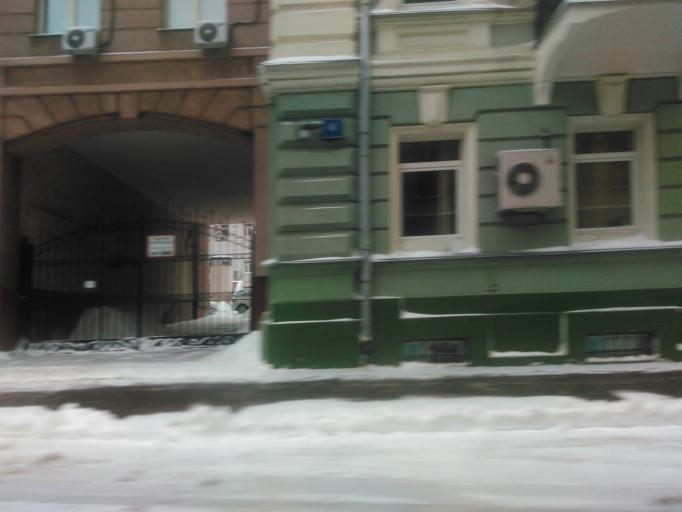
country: RU
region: Moscow
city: Moscow
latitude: 55.7745
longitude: 37.6306
